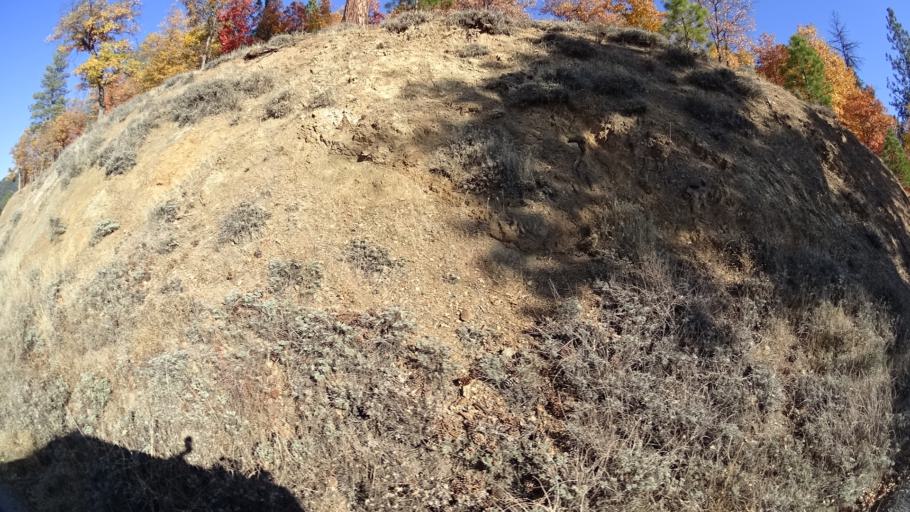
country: US
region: California
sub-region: Siskiyou County
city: Yreka
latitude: 41.6384
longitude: -122.9851
